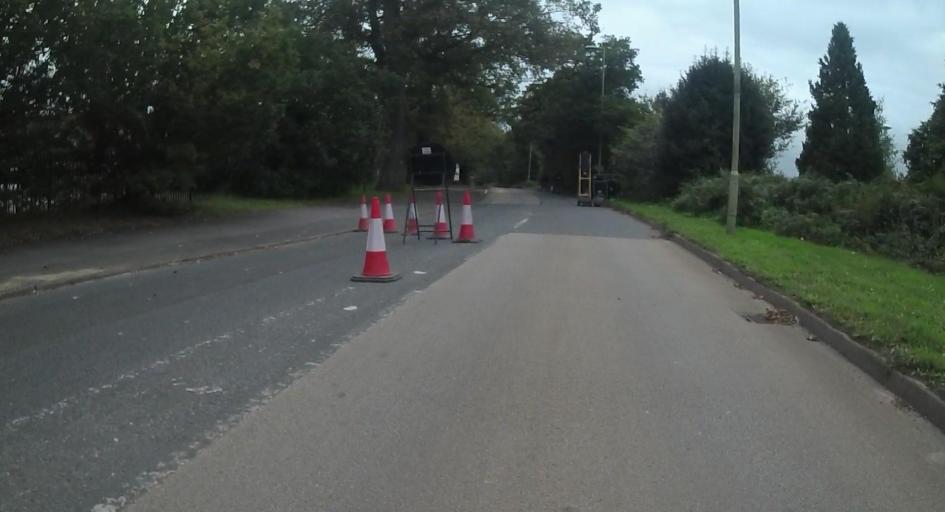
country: GB
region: England
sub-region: Hampshire
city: Fleet
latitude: 51.2790
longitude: -0.8635
